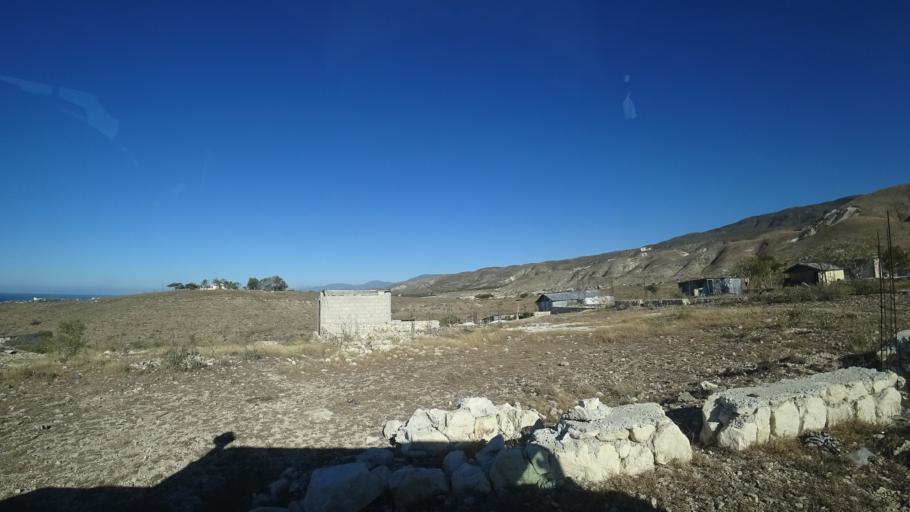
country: HT
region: Ouest
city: Cabaret
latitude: 18.6896
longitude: -72.3219
